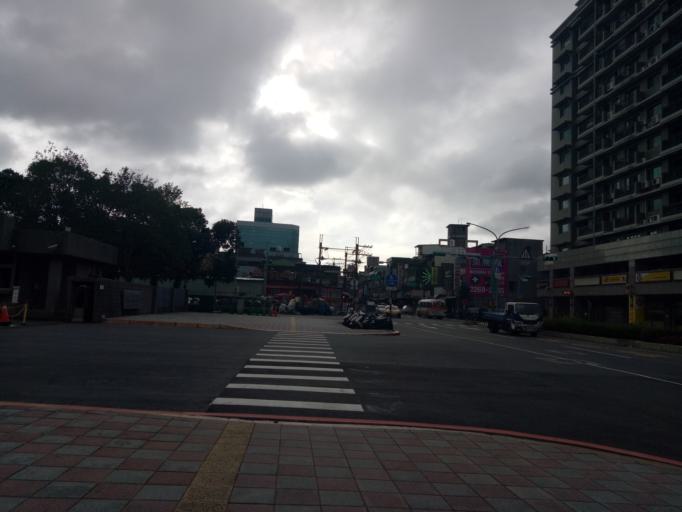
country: TW
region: Taipei
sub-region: Taipei
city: Banqiao
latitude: 24.9588
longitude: 121.4182
